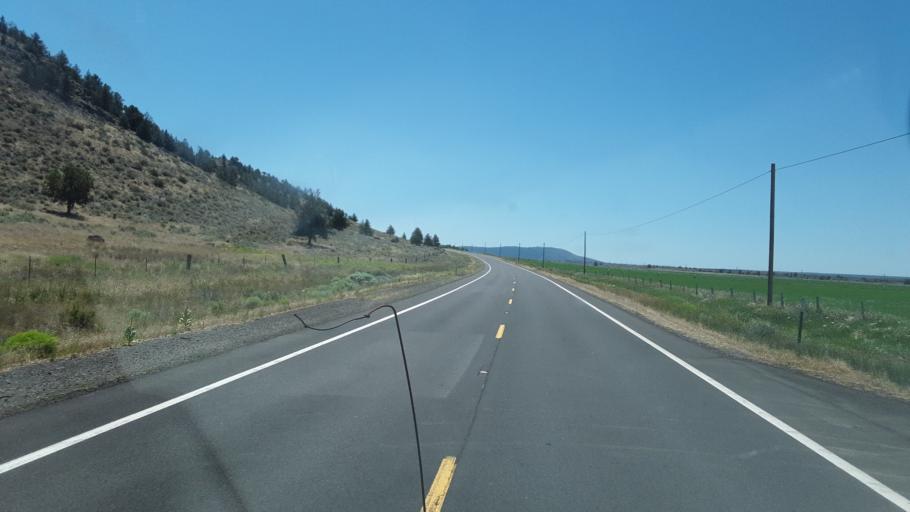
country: US
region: California
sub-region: Siskiyou County
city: Tulelake
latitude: 41.7502
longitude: -121.3020
